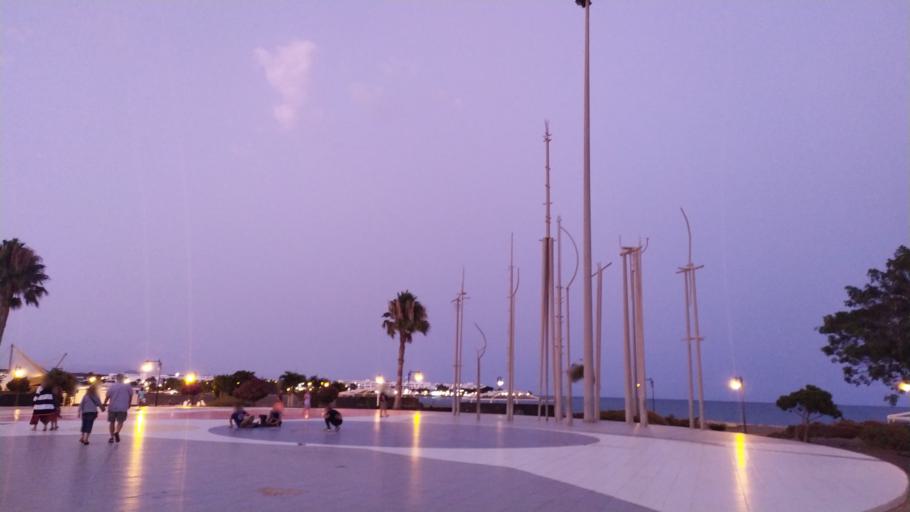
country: ES
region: Canary Islands
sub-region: Provincia de Las Palmas
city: Puerto del Carmen
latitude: 28.9253
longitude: -13.6381
